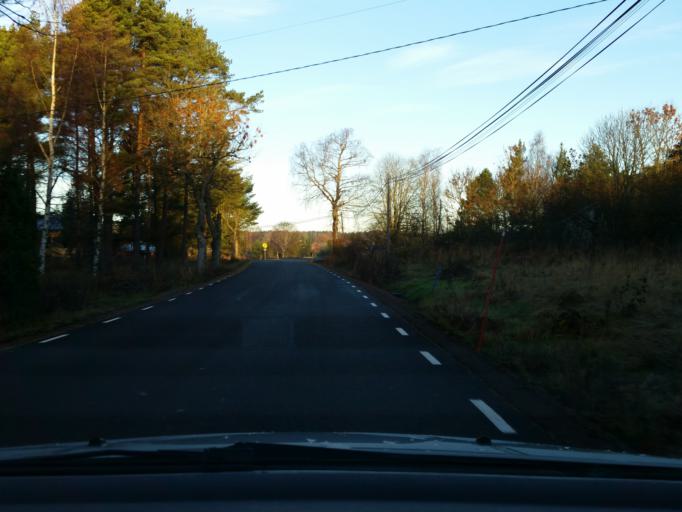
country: AX
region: Alands landsbygd
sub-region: Sund
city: Sund
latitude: 60.2390
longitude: 20.0721
